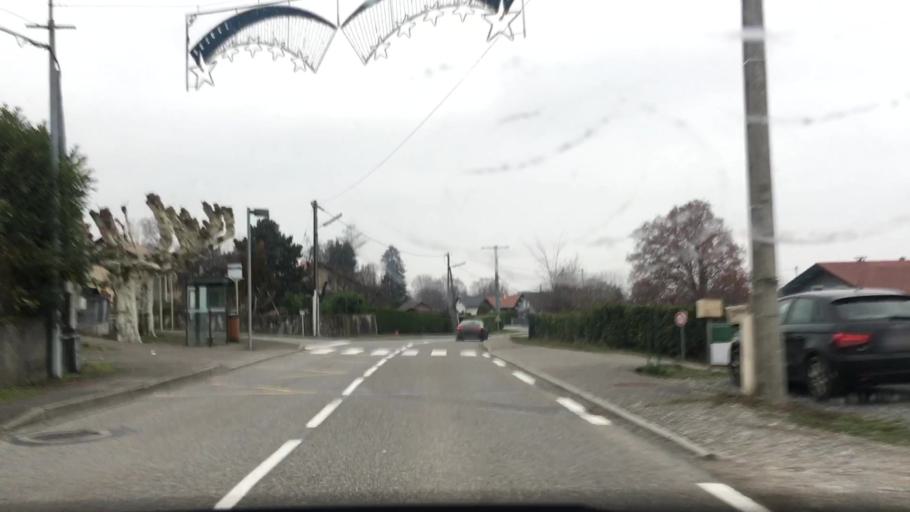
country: FR
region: Rhone-Alpes
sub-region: Departement de la Haute-Savoie
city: Publier
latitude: 46.3850
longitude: 6.5514
